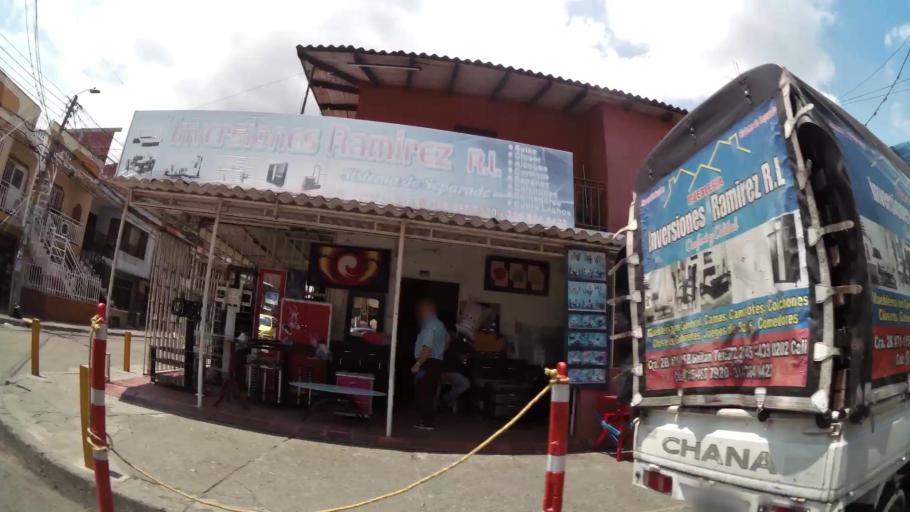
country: CO
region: Valle del Cauca
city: Cali
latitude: 3.4729
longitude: -76.4841
